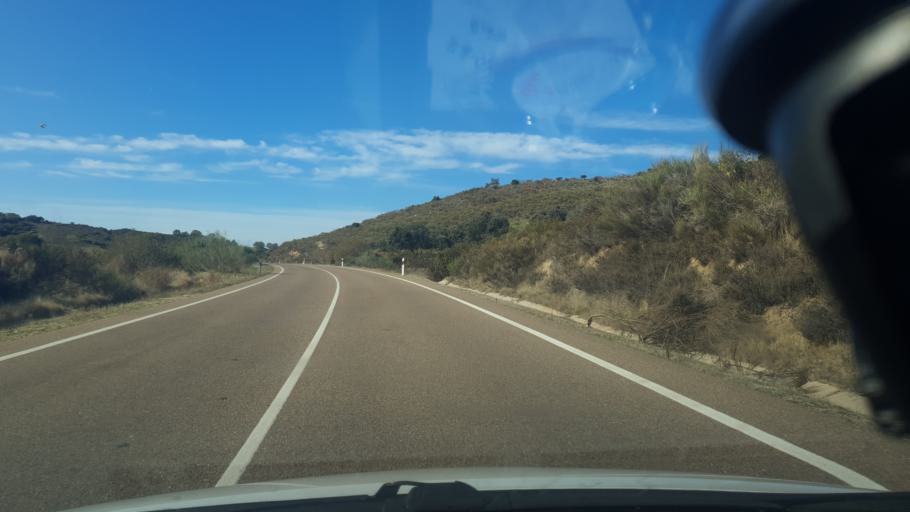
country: ES
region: Castille and Leon
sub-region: Provincia de Avila
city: Poyales del Hoyo
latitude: 40.1590
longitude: -5.1618
